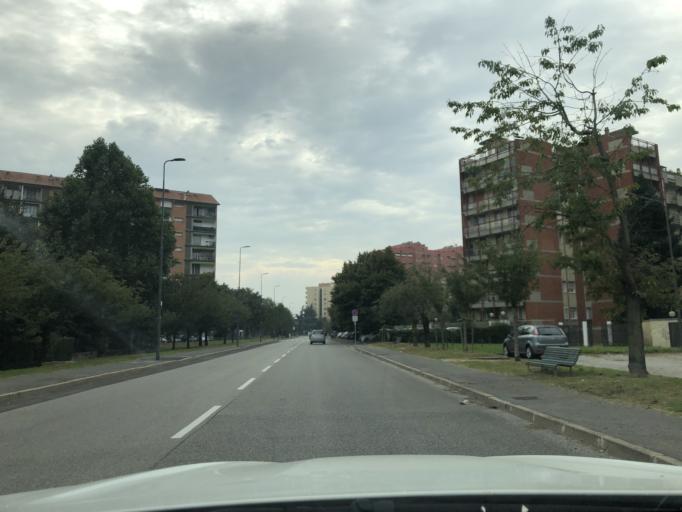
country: IT
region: Lombardy
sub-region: Citta metropolitana di Milano
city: Baranzate
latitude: 45.4912
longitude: 9.1182
